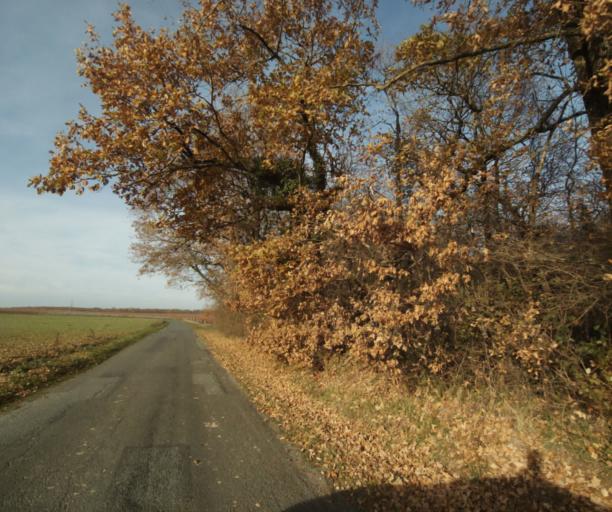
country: FR
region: Poitou-Charentes
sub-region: Departement de la Charente-Maritime
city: Chaniers
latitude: 45.7447
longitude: -0.5207
